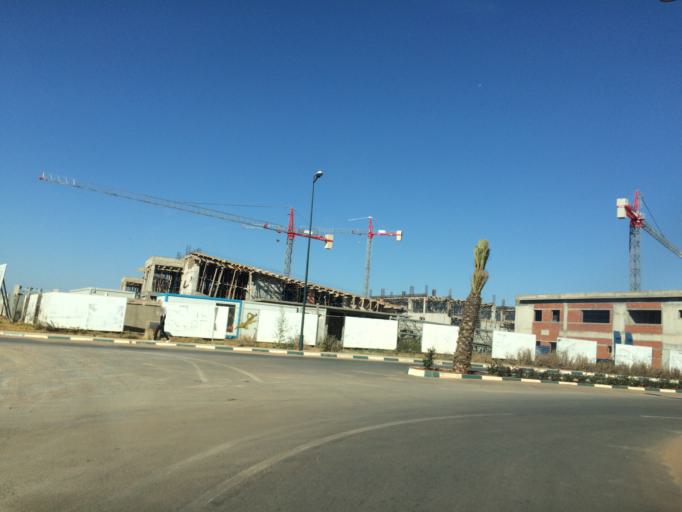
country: MA
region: Rabat-Sale-Zemmour-Zaer
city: Sale
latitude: 33.9877
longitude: -6.7278
